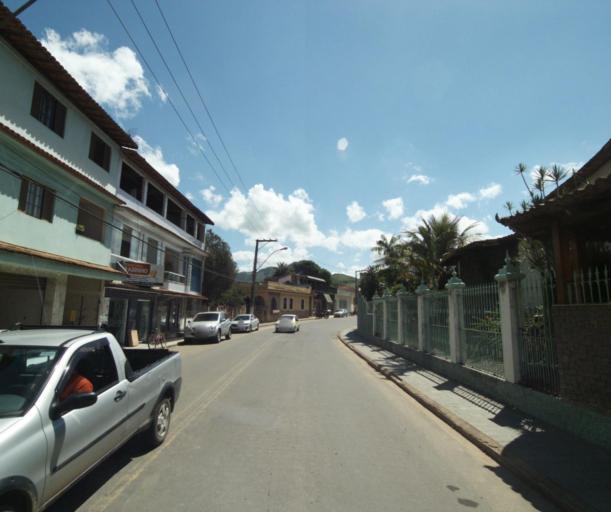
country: BR
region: Espirito Santo
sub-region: Mimoso Do Sul
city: Mimoso do Sul
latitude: -21.0650
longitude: -41.3609
